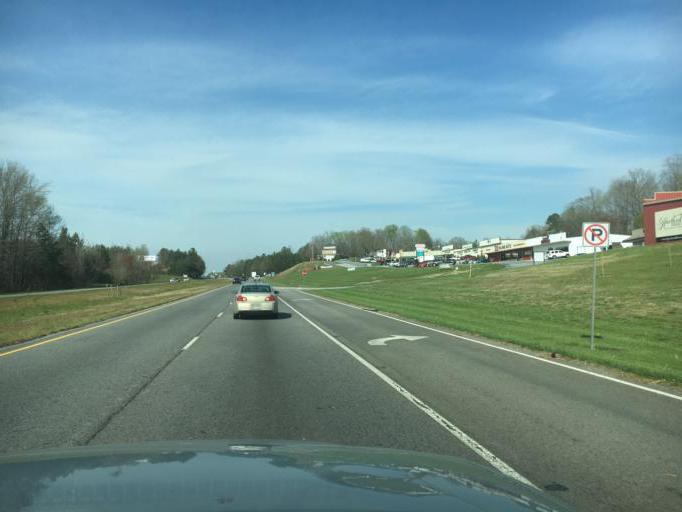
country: US
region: Georgia
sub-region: Banks County
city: Alto
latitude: 34.4734
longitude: -83.5938
